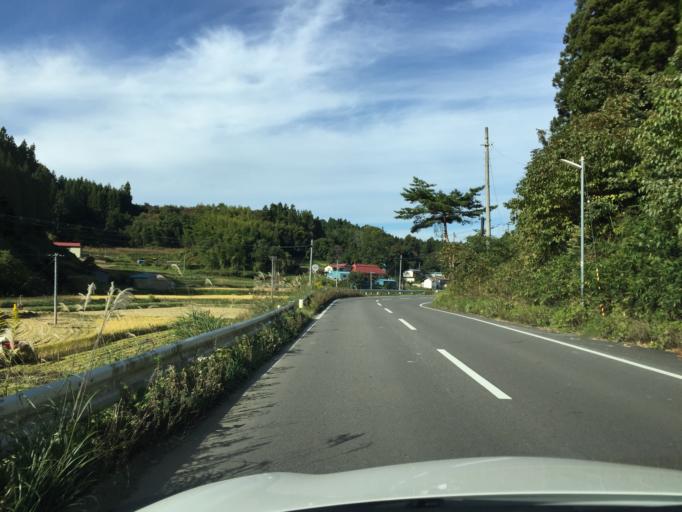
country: JP
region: Fukushima
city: Miharu
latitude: 37.3467
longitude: 140.5088
